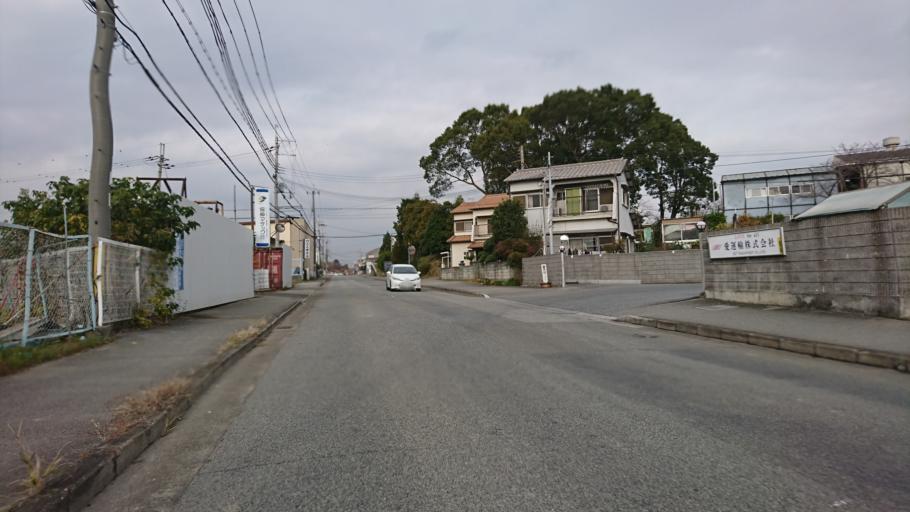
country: JP
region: Hyogo
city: Kakogawacho-honmachi
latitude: 34.7687
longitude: 134.8640
